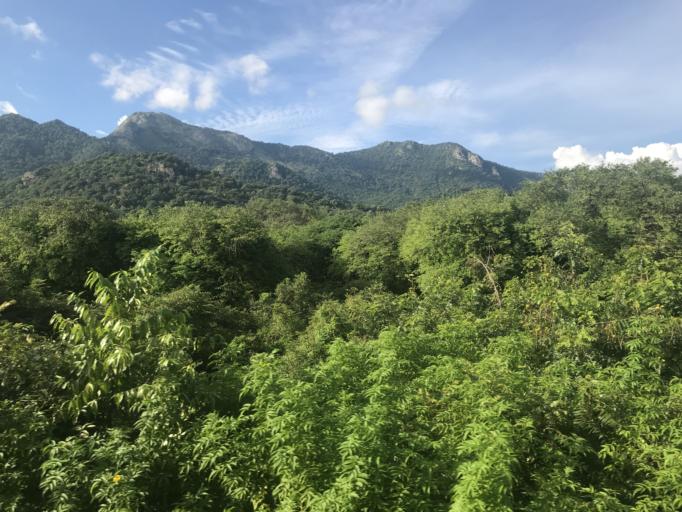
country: IN
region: Tamil Nadu
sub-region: Coimbatore
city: Madukkarai
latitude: 10.8761
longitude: 76.8547
